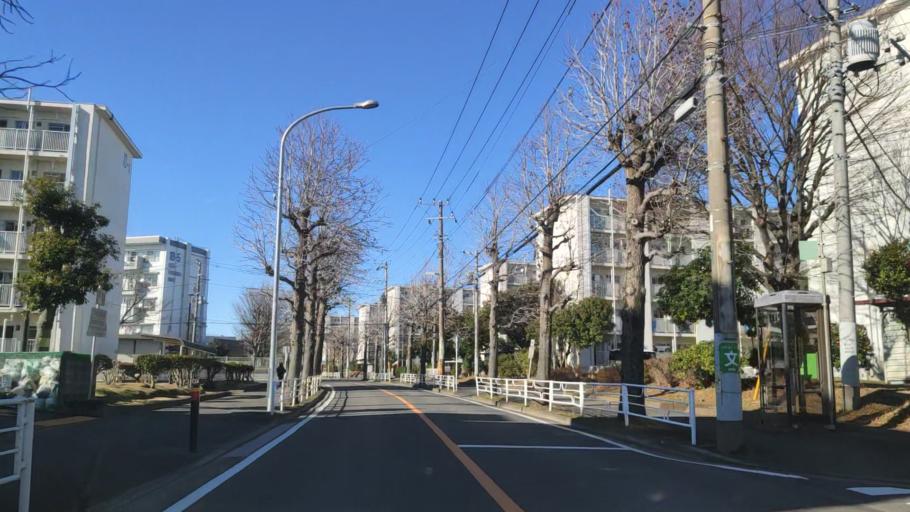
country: JP
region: Kanagawa
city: Minami-rinkan
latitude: 35.4979
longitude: 139.5319
